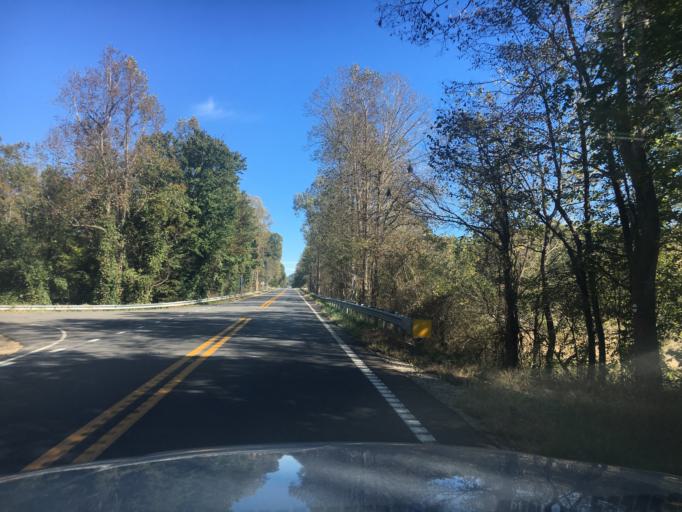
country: US
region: North Carolina
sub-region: Burke County
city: Glen Alpine
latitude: 35.5850
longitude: -81.8369
